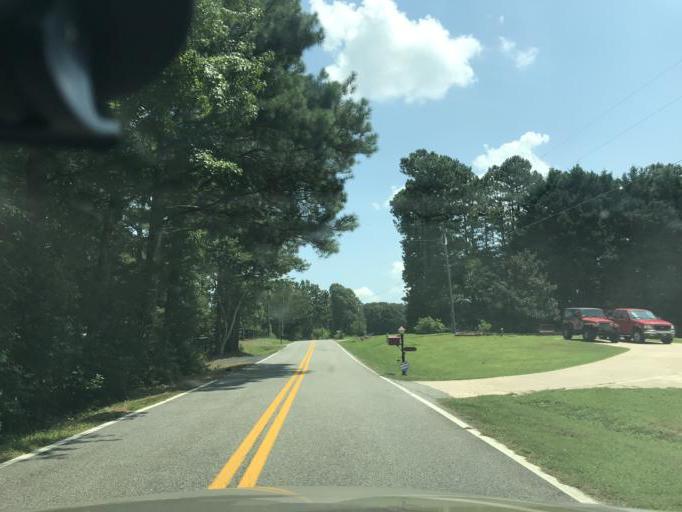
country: US
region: Georgia
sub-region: Forsyth County
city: Cumming
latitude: 34.3151
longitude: -84.1581
